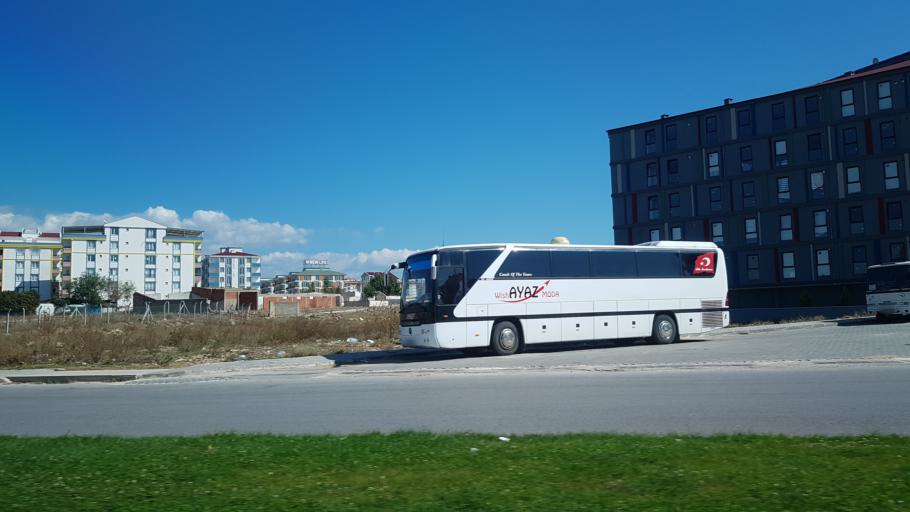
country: TR
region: Kirklareli
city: Kirklareli
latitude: 41.7504
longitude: 27.2192
